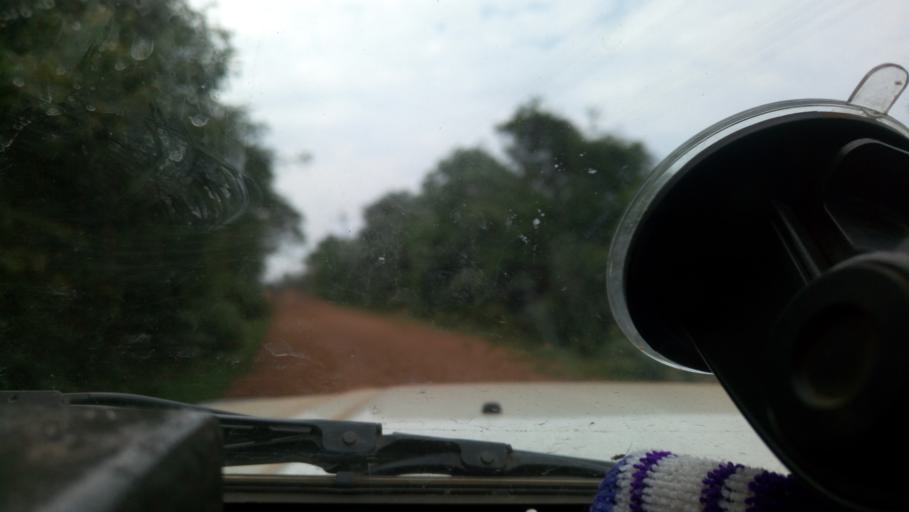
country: KE
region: Kericho
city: Litein
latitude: -0.5840
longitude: 35.2068
